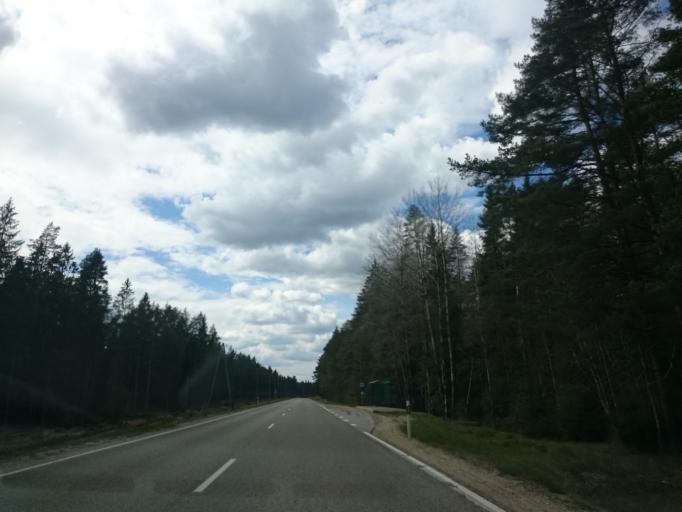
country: LV
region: Talsu Rajons
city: Sabile
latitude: 56.9515
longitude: 22.2804
